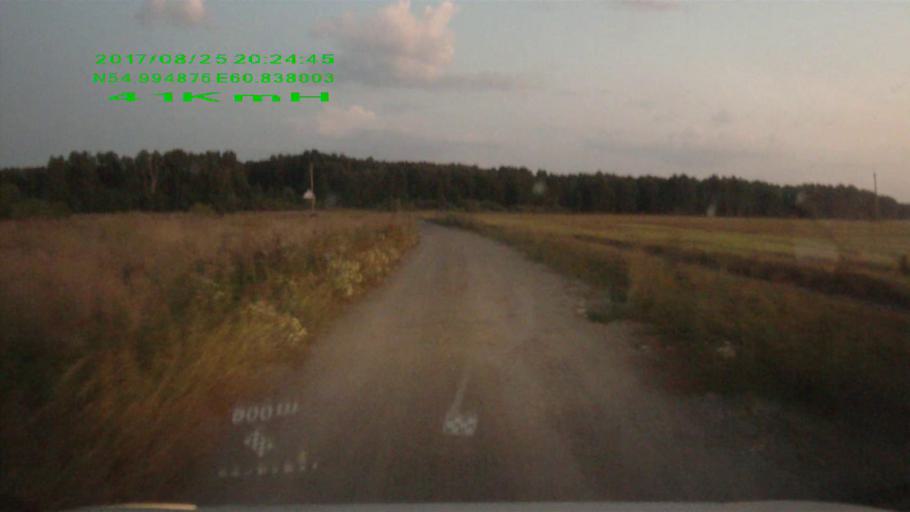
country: RU
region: Chelyabinsk
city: Timiryazevskiy
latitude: 54.9949
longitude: 60.8380
